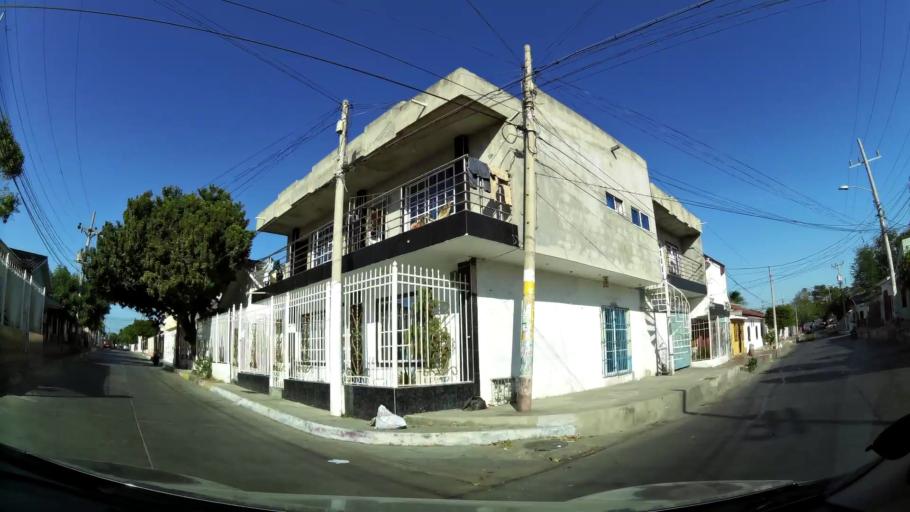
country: CO
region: Atlantico
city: Barranquilla
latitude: 10.9618
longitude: -74.7862
